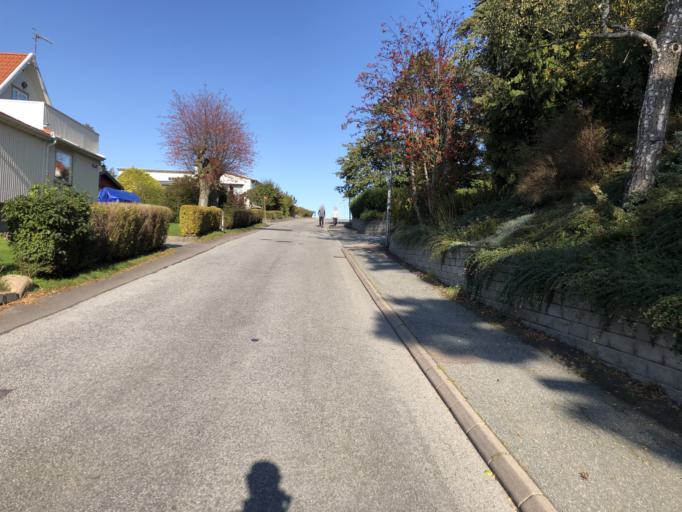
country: SE
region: Vaestra Goetaland
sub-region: Goteborg
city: Billdal
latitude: 57.6223
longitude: 11.8902
